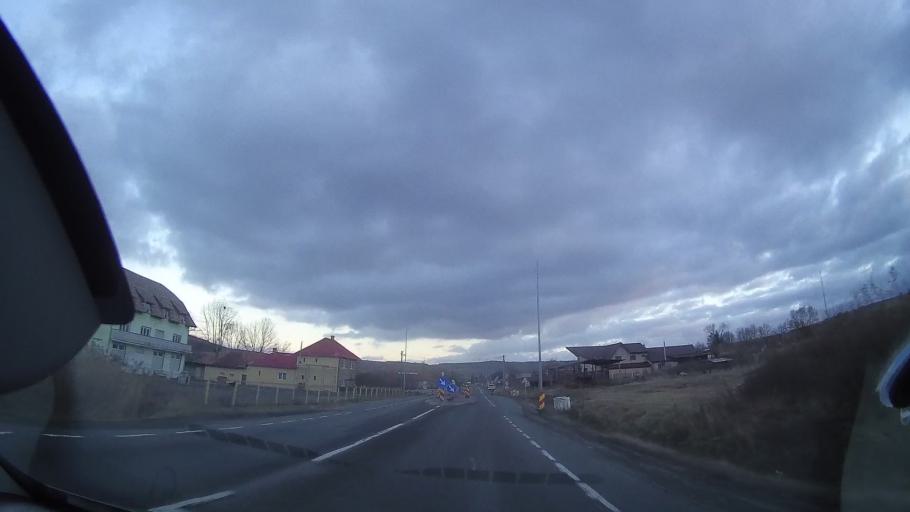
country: RO
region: Cluj
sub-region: Comuna Izvoru Crisului
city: Izvoru Crisului
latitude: 46.8173
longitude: 23.1756
